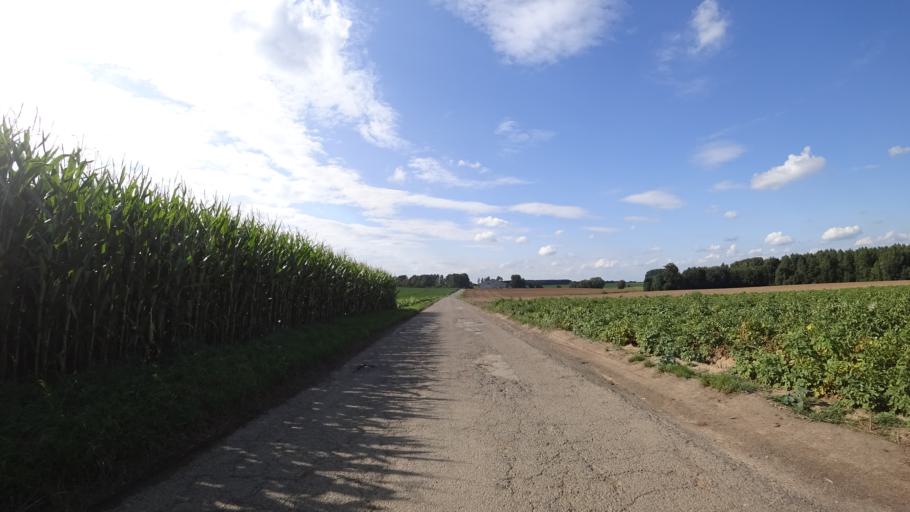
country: BE
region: Wallonia
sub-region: Province de Namur
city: Sombreffe
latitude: 50.5487
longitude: 4.6424
